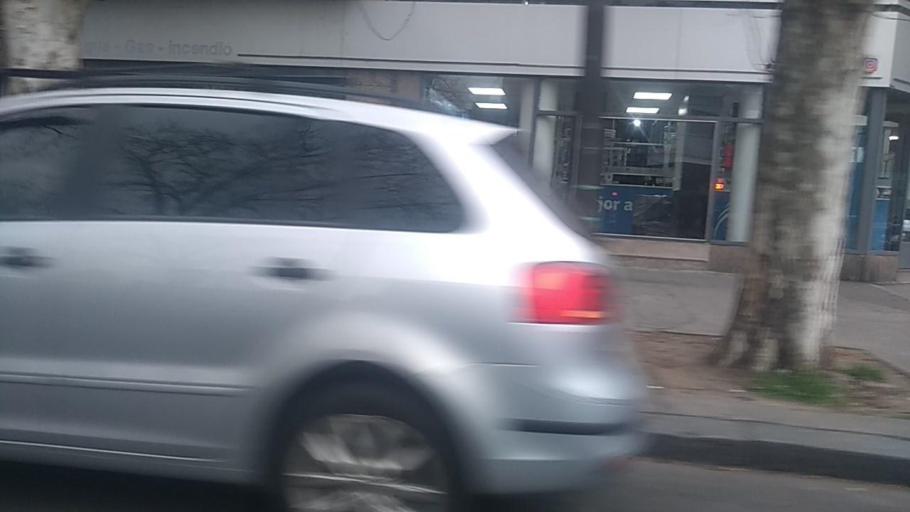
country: AR
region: Buenos Aires F.D.
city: Villa Santa Rita
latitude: -34.5982
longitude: -58.4994
